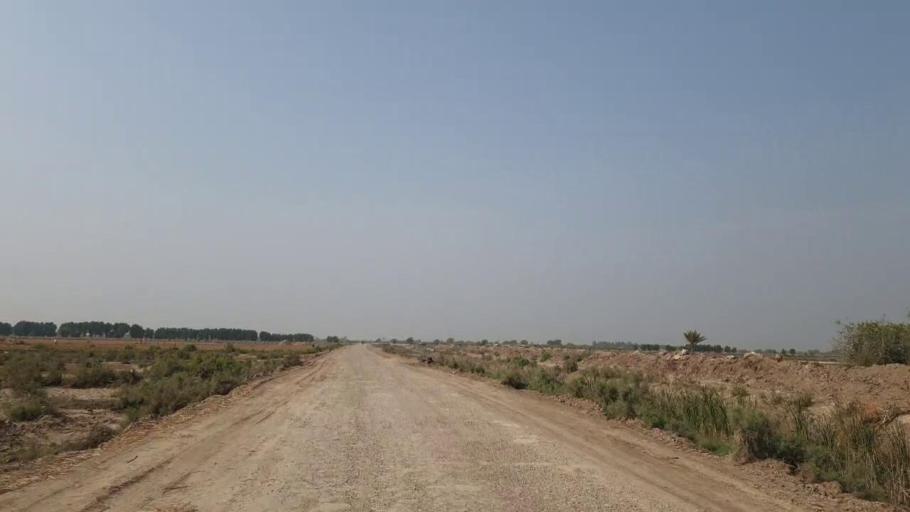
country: PK
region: Sindh
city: Tando Muhammad Khan
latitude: 24.9700
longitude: 68.5098
